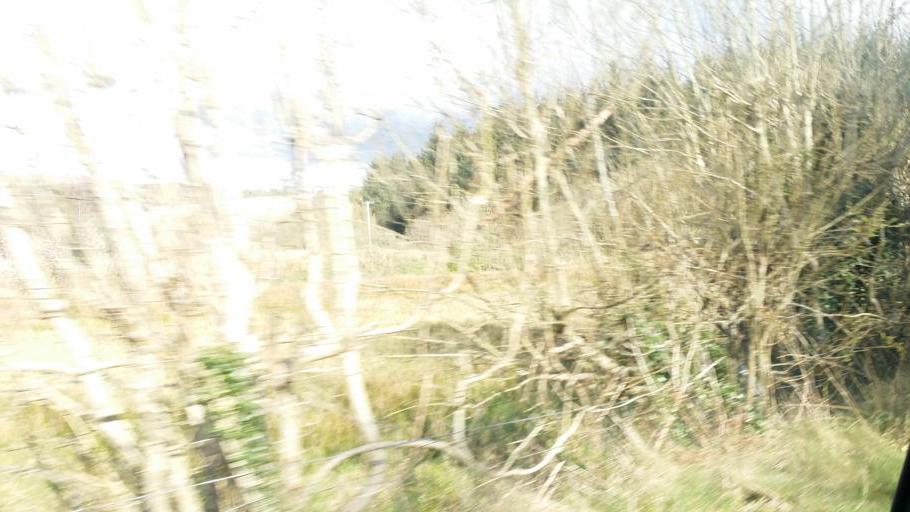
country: IE
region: Connaught
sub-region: County Leitrim
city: Manorhamilton
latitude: 54.3313
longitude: -8.2146
